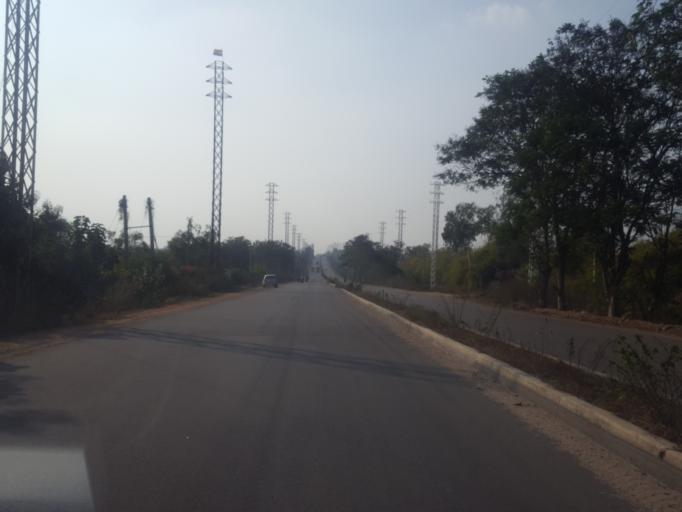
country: IN
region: Telangana
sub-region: Medak
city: Serilingampalle
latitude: 17.4184
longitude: 78.2451
